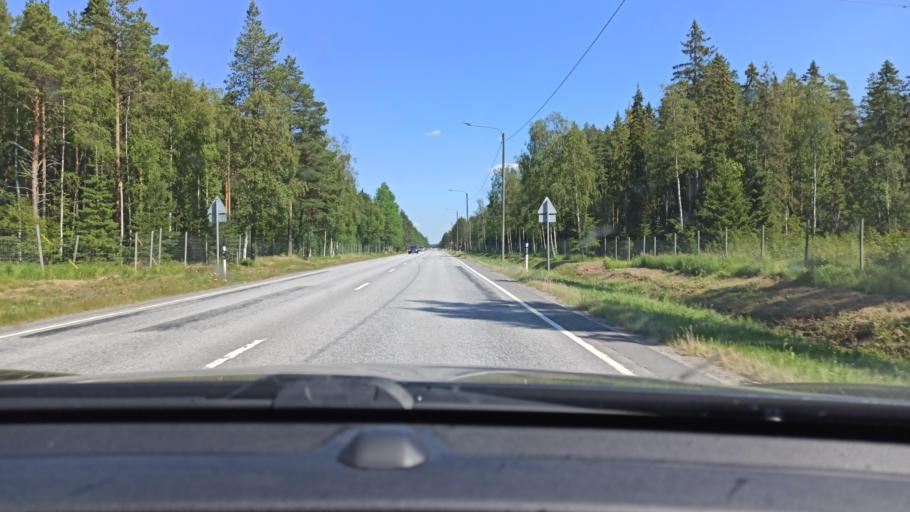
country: FI
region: Northern Ostrobothnia
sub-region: Raahe
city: Ruukki
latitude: 64.7228
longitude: 25.0005
